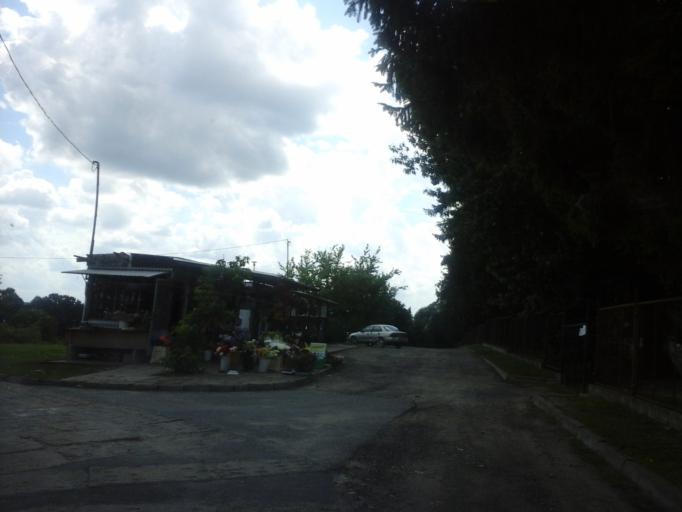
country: PL
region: West Pomeranian Voivodeship
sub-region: Powiat choszczenski
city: Recz
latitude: 53.2629
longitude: 15.5426
